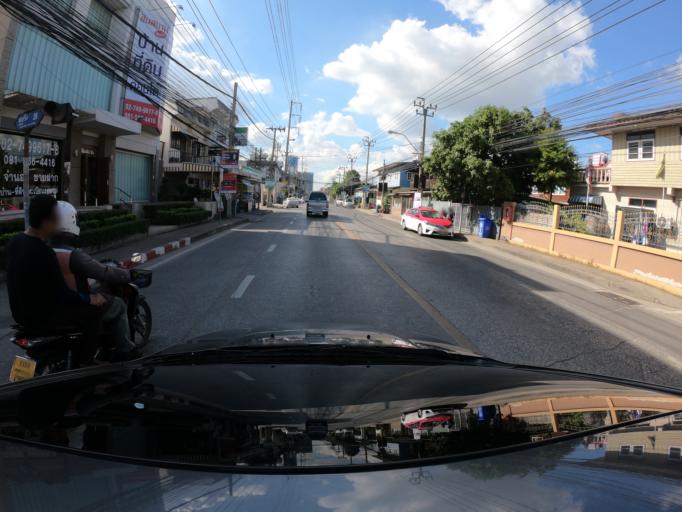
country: TH
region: Bangkok
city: Bang Na
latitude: 13.6541
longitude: 100.6126
